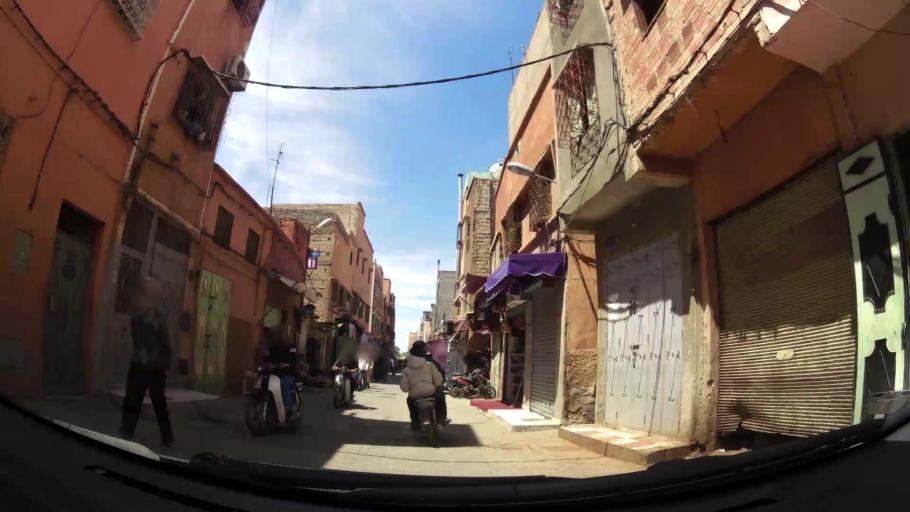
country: MA
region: Marrakech-Tensift-Al Haouz
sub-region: Marrakech
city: Marrakesh
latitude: 31.6190
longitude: -7.9705
